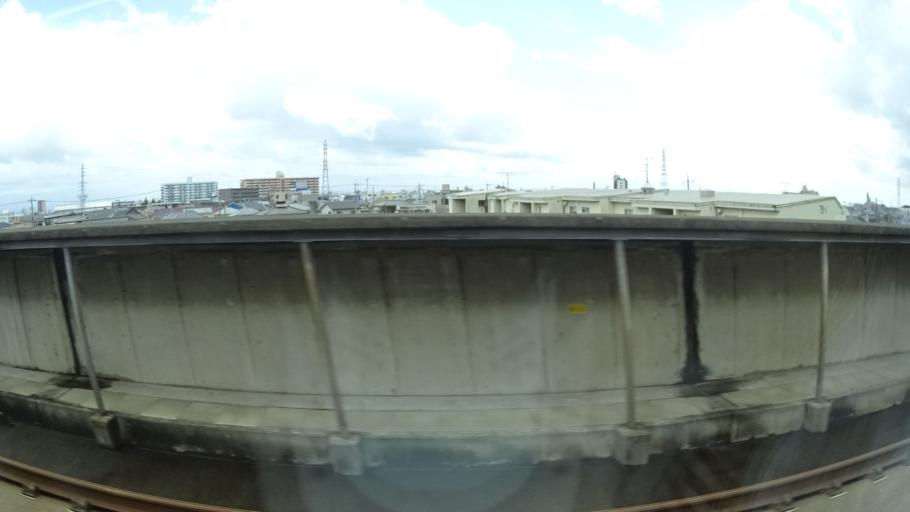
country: JP
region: Gunma
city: Takasaki
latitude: 36.3135
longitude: 139.0142
